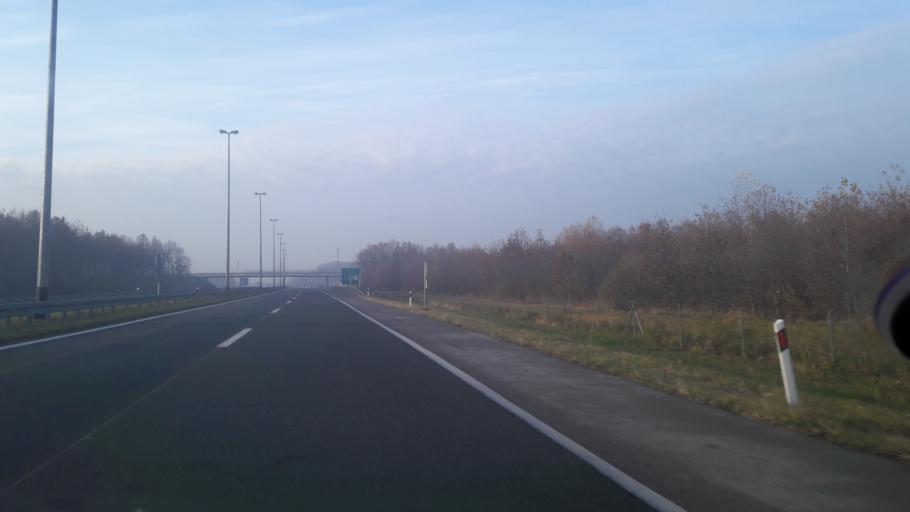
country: HR
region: Osjecko-Baranjska
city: Vuka
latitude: 45.4747
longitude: 18.4849
